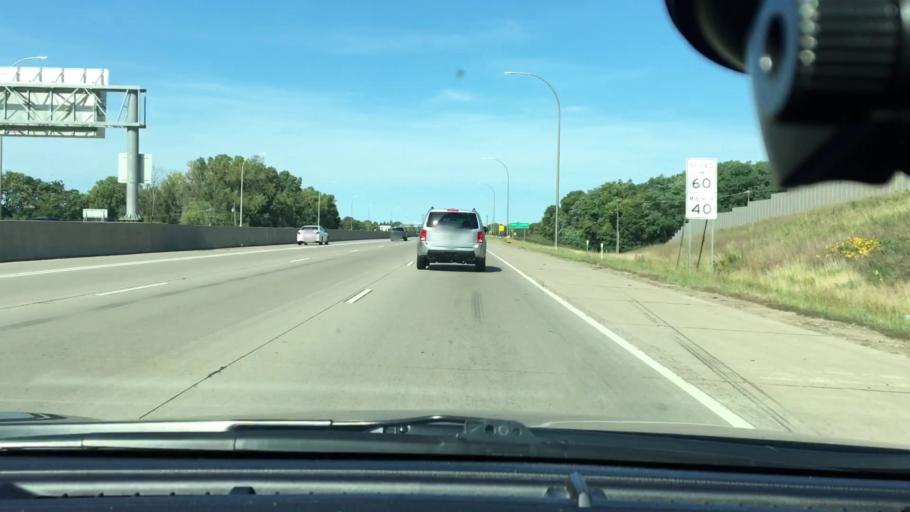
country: US
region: Minnesota
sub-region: Ramsey County
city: Little Canada
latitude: 45.0045
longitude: -93.0894
